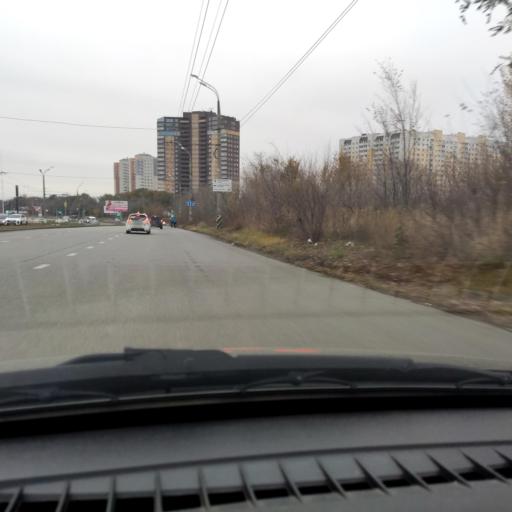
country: RU
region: Samara
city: Tol'yatti
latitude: 53.5102
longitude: 49.2560
